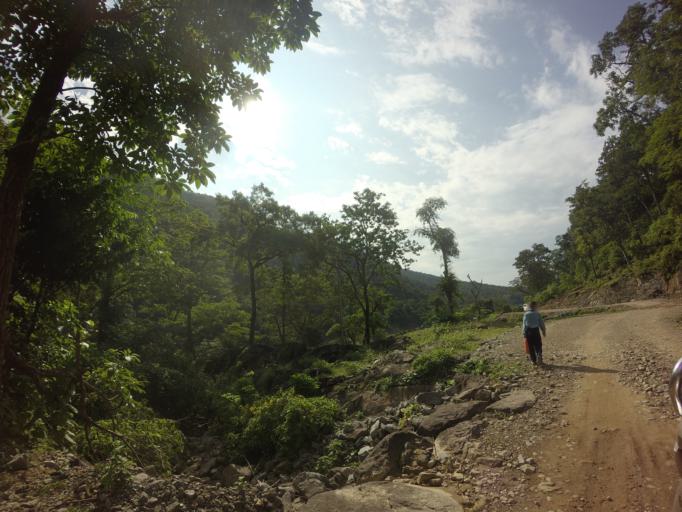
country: NP
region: Far Western
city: Tikapur
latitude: 28.6542
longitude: 81.2868
